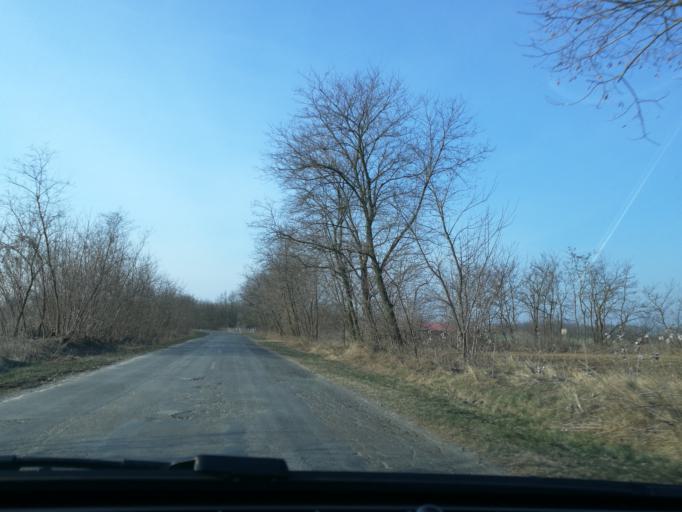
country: HU
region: Szabolcs-Szatmar-Bereg
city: Levelek
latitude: 48.0377
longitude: 21.9760
